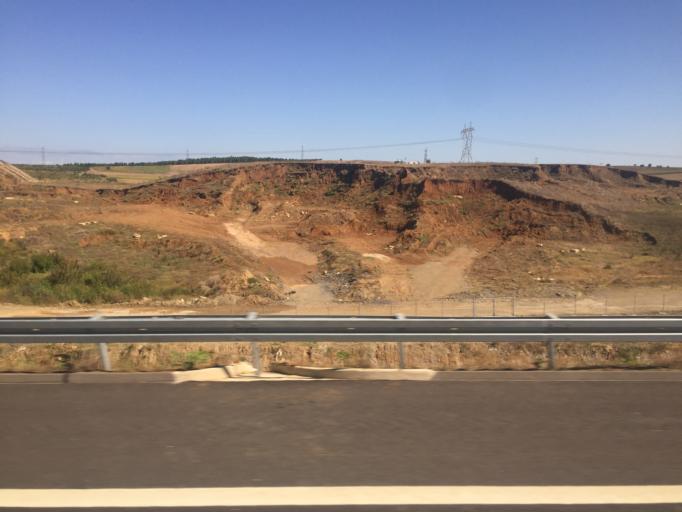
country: TR
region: Bursa
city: Mahmudiye
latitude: 40.2739
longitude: 28.5904
